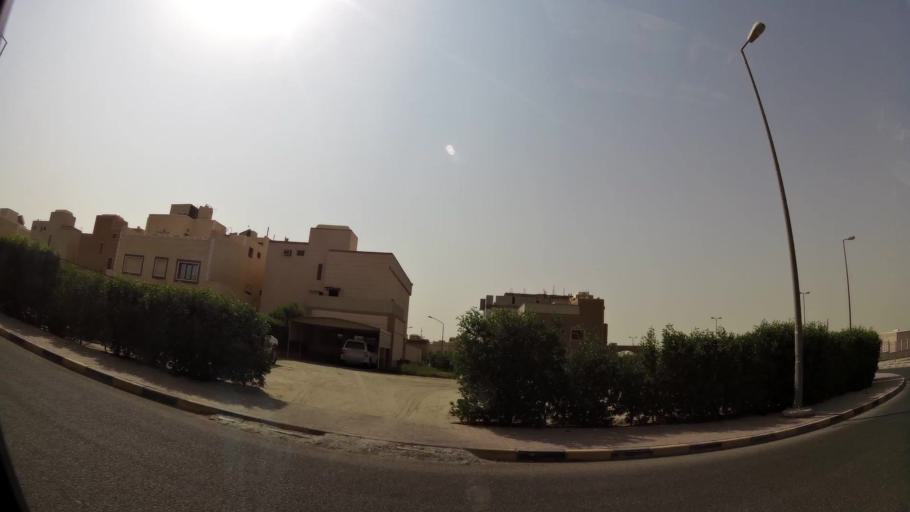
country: KW
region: Muhafazat al Jahra'
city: Al Jahra'
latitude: 29.3197
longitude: 47.7373
